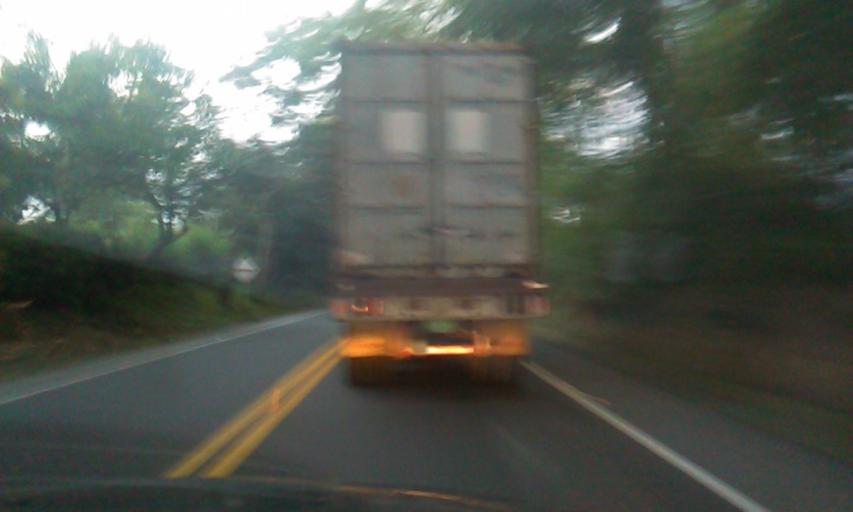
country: CO
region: Quindio
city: La Tebaida
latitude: 4.4483
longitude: -75.8077
